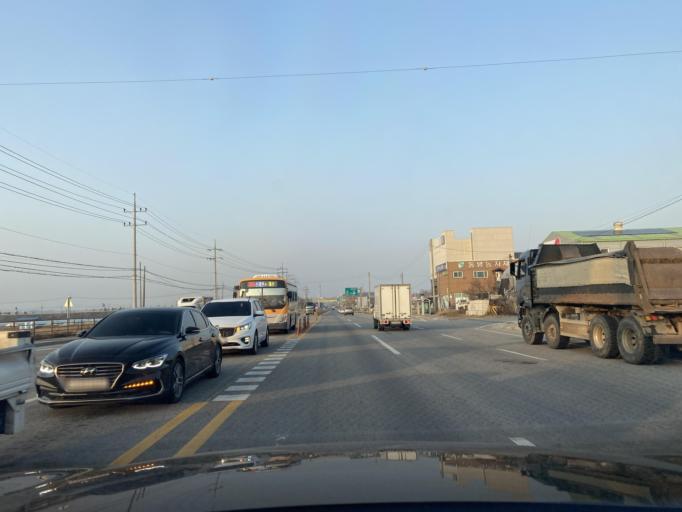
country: KR
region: Chungcheongnam-do
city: Yesan
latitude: 36.6989
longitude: 126.8291
